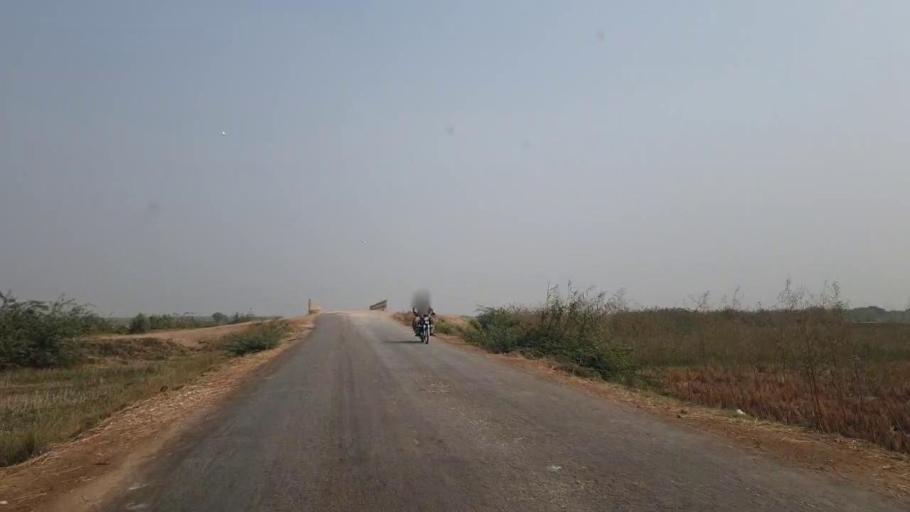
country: PK
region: Sindh
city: Matli
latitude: 25.0603
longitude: 68.6445
